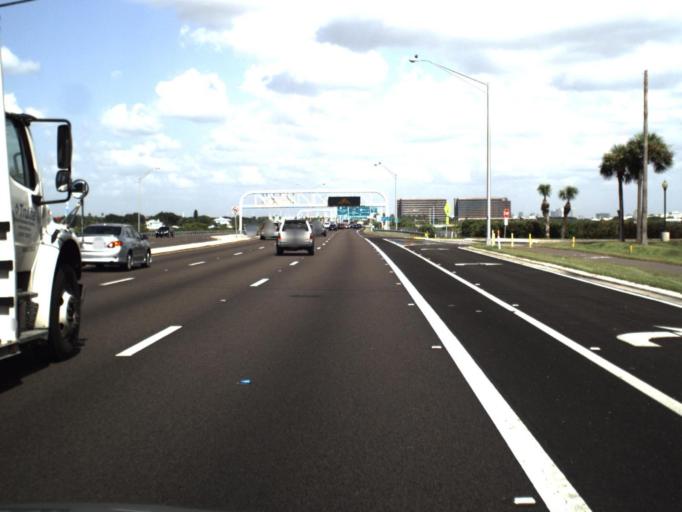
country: US
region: Florida
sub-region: Hillsborough County
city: Town 'n' Country
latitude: 27.9674
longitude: -82.5668
